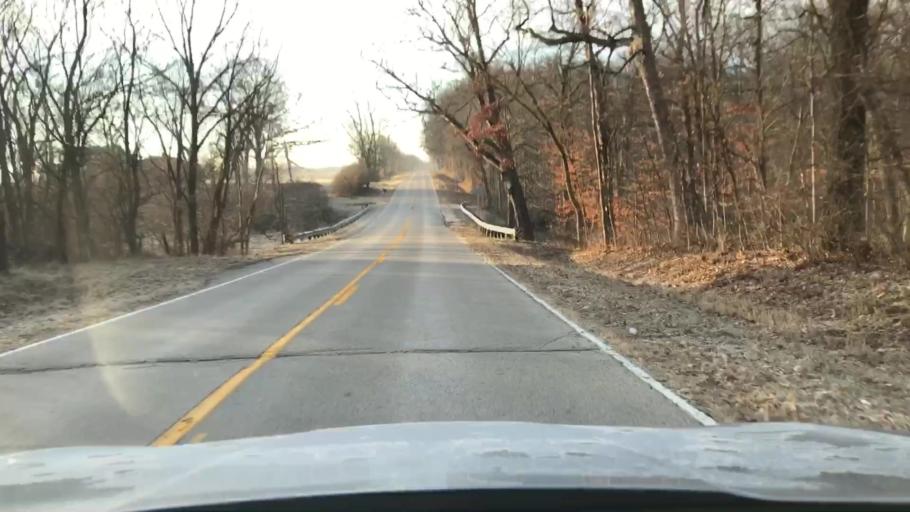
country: US
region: Illinois
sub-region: McLean County
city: Hudson
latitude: 40.6395
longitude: -88.9182
